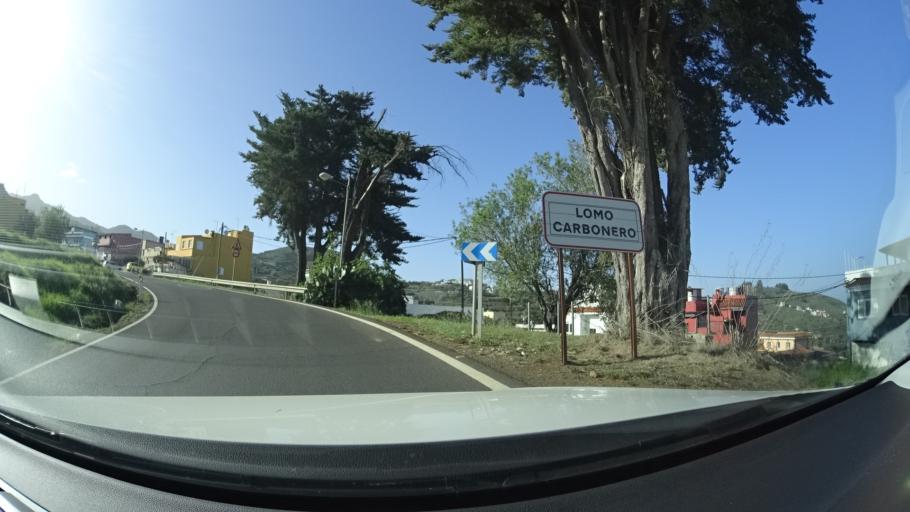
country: ES
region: Canary Islands
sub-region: Provincia de Las Palmas
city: Vega de San Mateo
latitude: 28.0254
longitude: -15.5444
